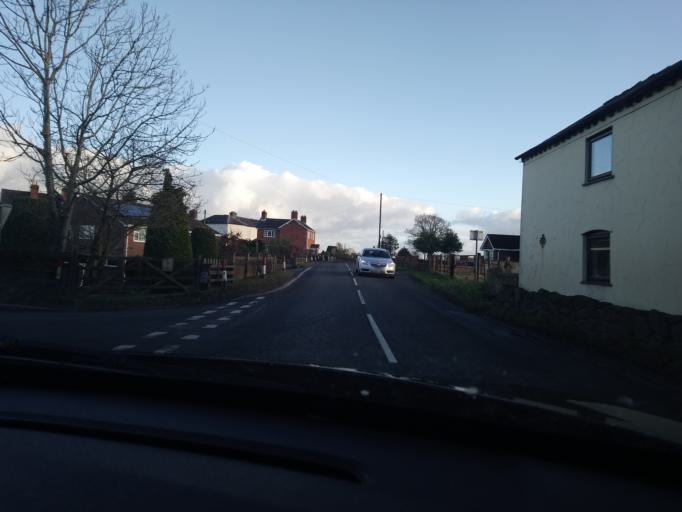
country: GB
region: England
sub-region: Shropshire
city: Petton
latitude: 52.8944
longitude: -2.7965
